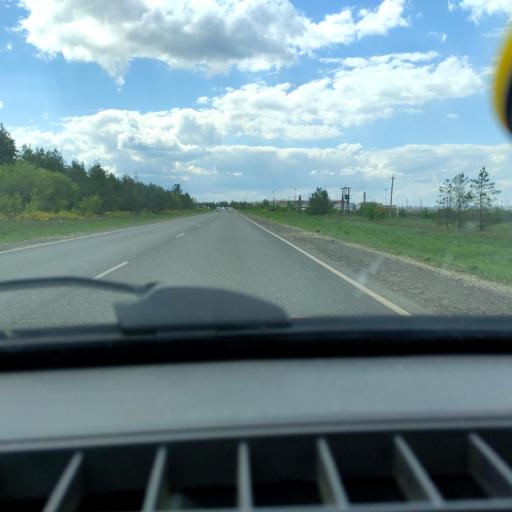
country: RU
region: Samara
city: Zhigulevsk
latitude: 53.5753
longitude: 49.5572
